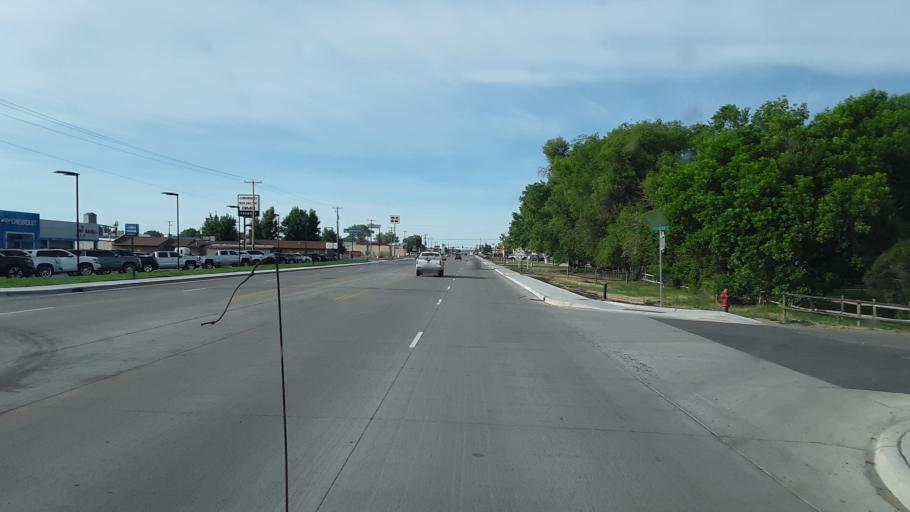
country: US
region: Wyoming
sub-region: Fremont County
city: Riverton
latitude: 43.0398
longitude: -108.3807
